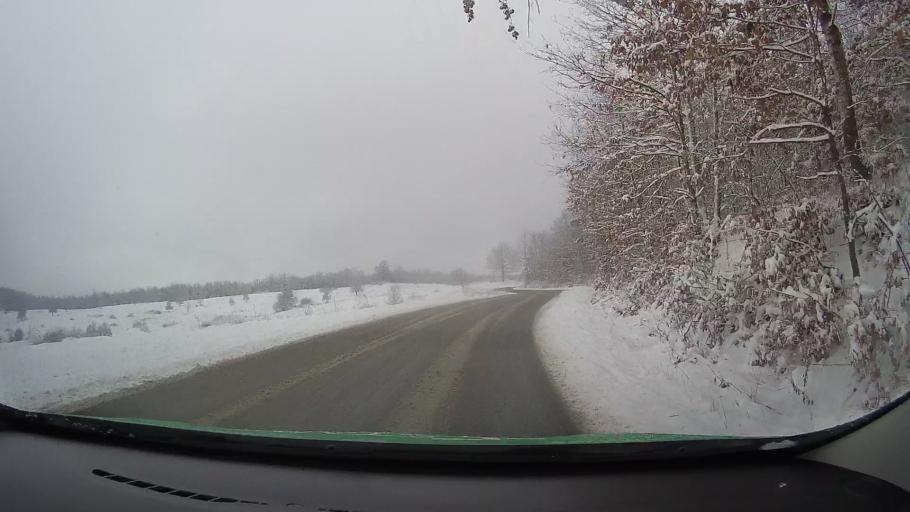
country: RO
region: Hunedoara
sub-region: Comuna Teliucu Inferior
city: Teliucu Inferior
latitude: 45.6832
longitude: 22.9110
